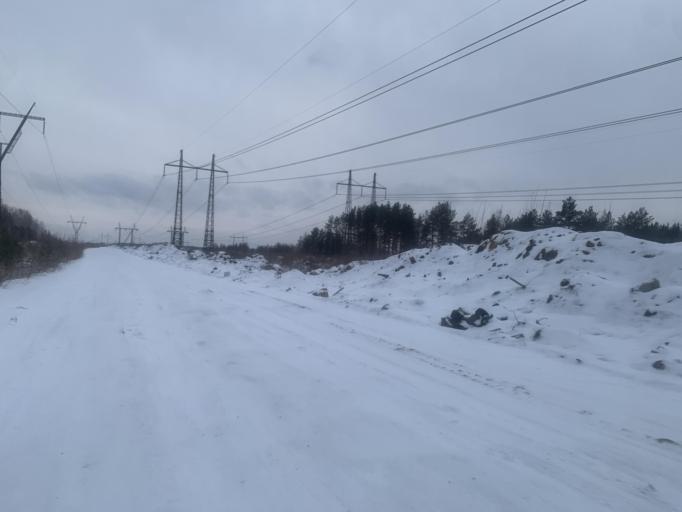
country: RU
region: Chelyabinsk
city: Roshchino
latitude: 55.1962
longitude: 61.2610
